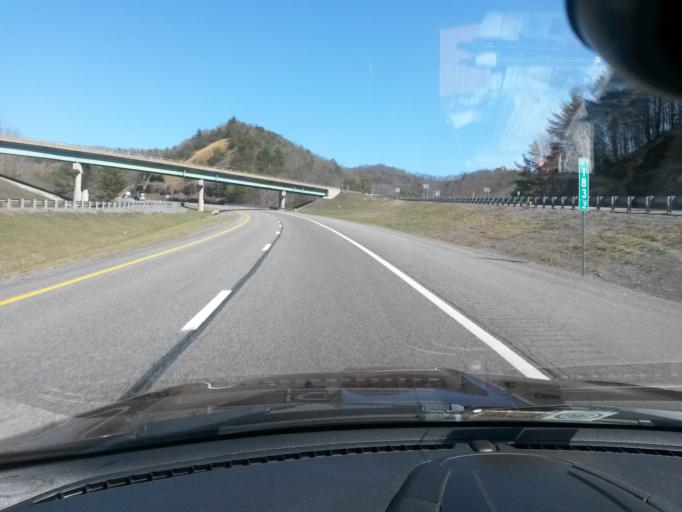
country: US
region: West Virginia
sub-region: Greenbrier County
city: White Sulphur Springs
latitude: 37.7822
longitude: -80.2341
